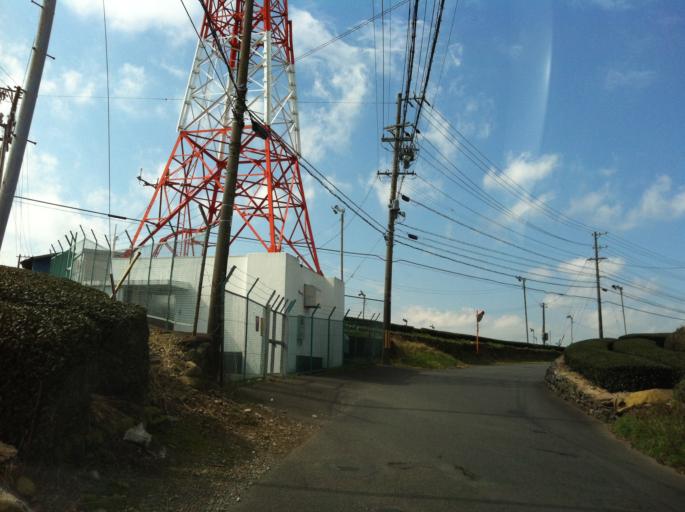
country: JP
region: Shizuoka
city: Kanaya
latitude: 34.8118
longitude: 138.1289
